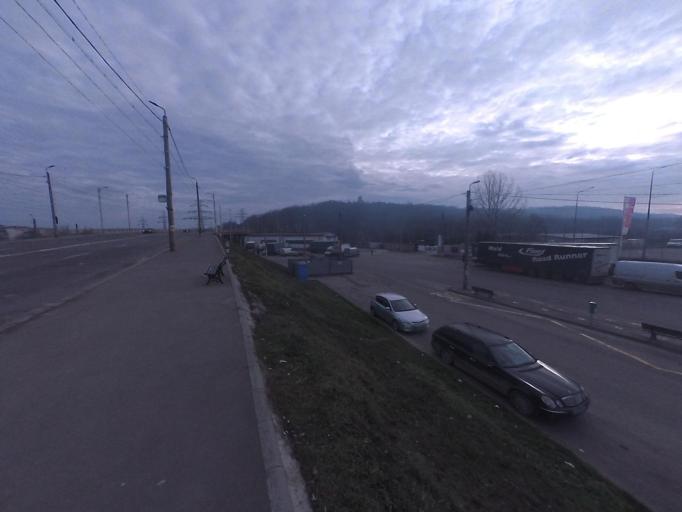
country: RO
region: Iasi
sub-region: Comuna Ciurea
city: Lunca Cetatuii
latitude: 47.1338
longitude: 27.5752
